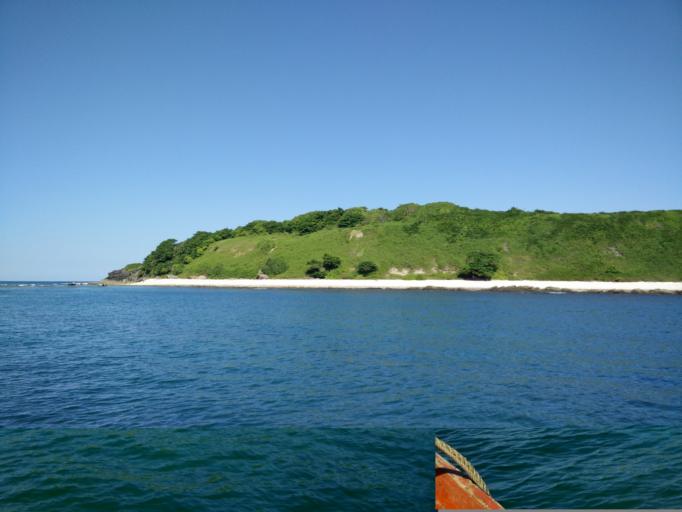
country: MM
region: Ayeyarwady
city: Pathein
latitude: 16.8854
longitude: 94.2703
